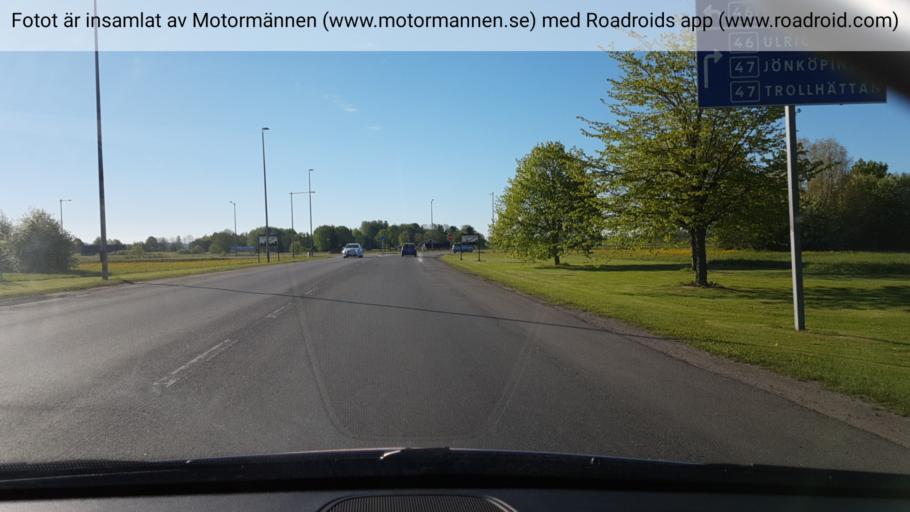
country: SE
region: Vaestra Goetaland
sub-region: Falkopings Kommun
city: Falkoeping
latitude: 58.1692
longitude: 13.5823
